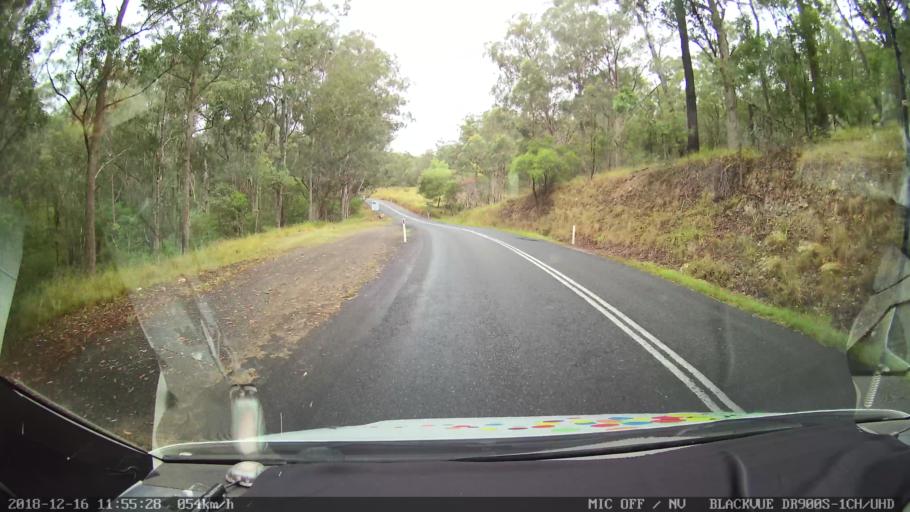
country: AU
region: New South Wales
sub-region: Tenterfield Municipality
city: Carrolls Creek
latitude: -28.9129
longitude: 152.2915
